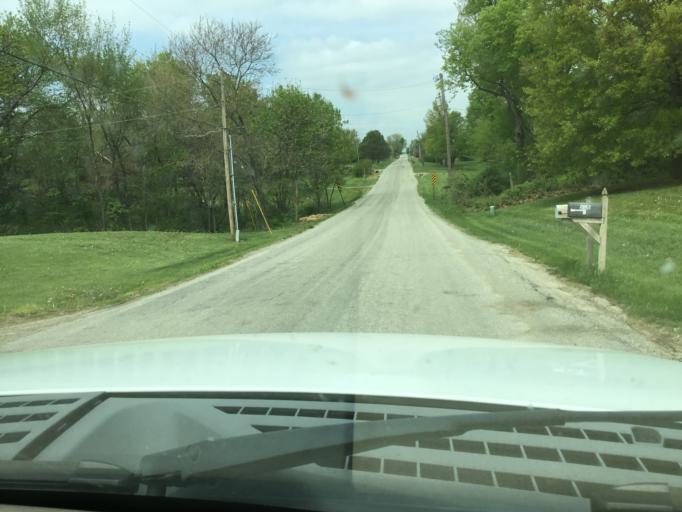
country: US
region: Kansas
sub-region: Shawnee County
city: Topeka
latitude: 38.9746
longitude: -95.5863
